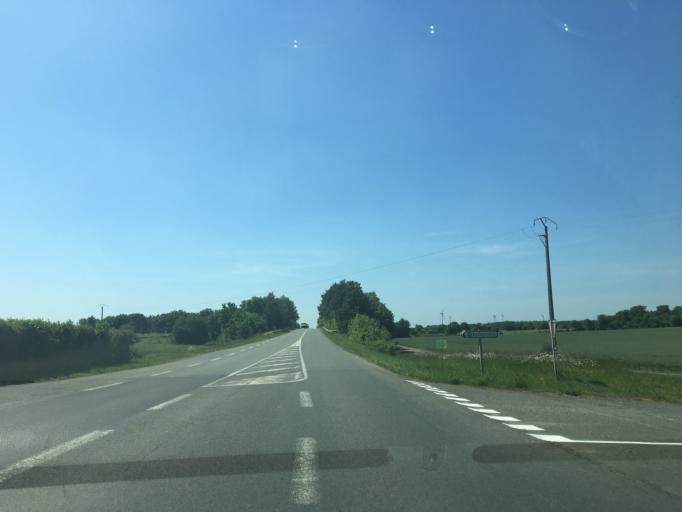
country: FR
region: Poitou-Charentes
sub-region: Departement des Deux-Sevres
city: Beauvoir-sur-Niort
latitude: 46.0781
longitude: -0.5271
